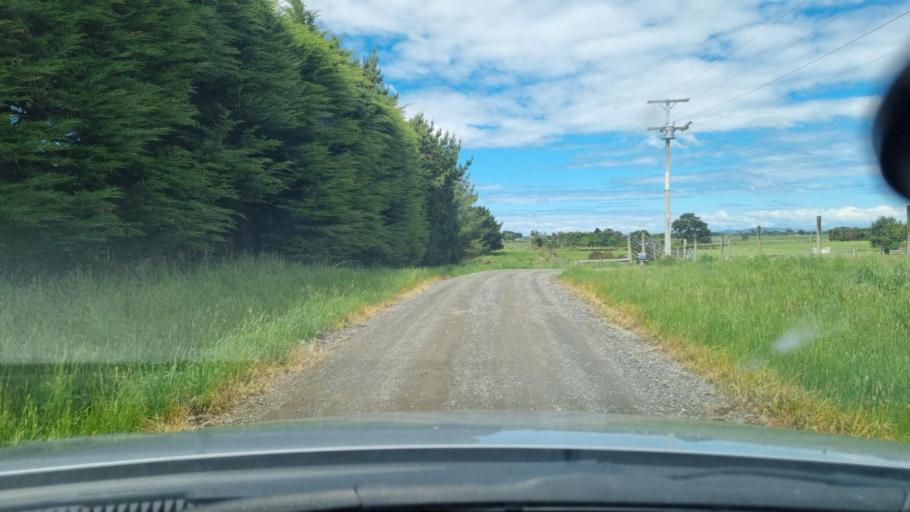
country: NZ
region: Southland
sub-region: Invercargill City
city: Invercargill
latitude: -46.3709
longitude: 168.3237
